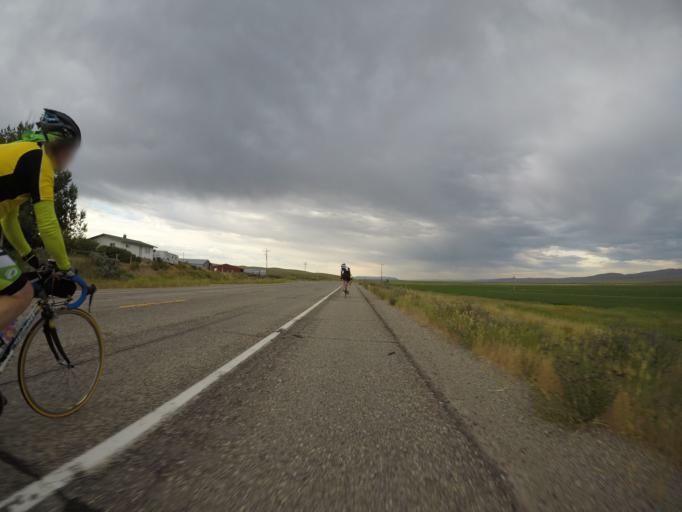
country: US
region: Utah
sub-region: Rich County
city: Randolph
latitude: 41.9785
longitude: -110.9431
